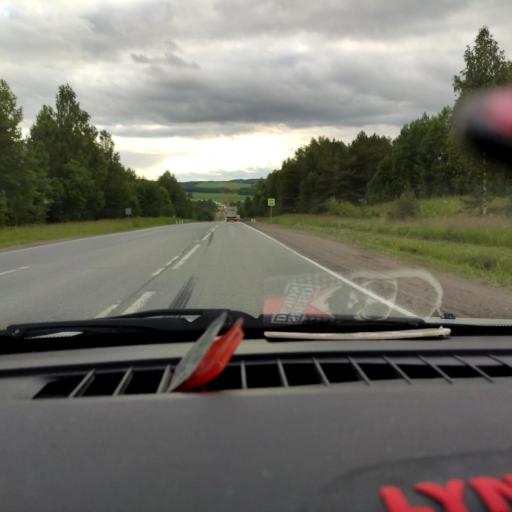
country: RU
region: Perm
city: Nytva
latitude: 57.9842
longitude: 55.2121
